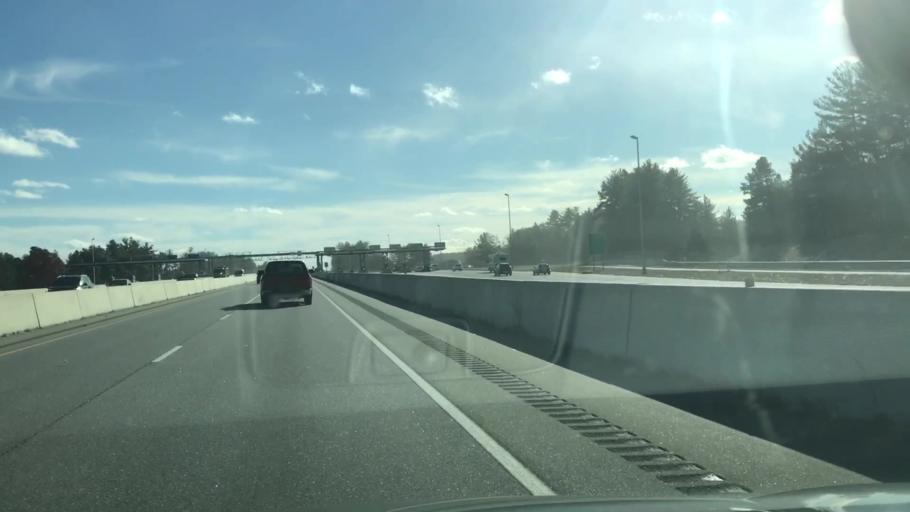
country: US
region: New Hampshire
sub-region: Merrimack County
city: Hooksett
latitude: 43.0875
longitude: -71.4743
